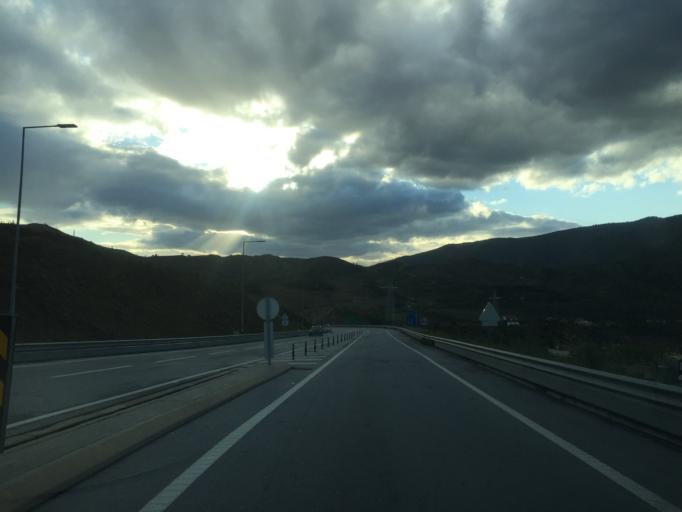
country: PT
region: Guarda
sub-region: Vila Nova de Foz Coa
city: Vila Nova de Foz Coa
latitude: 41.1268
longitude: -7.1257
